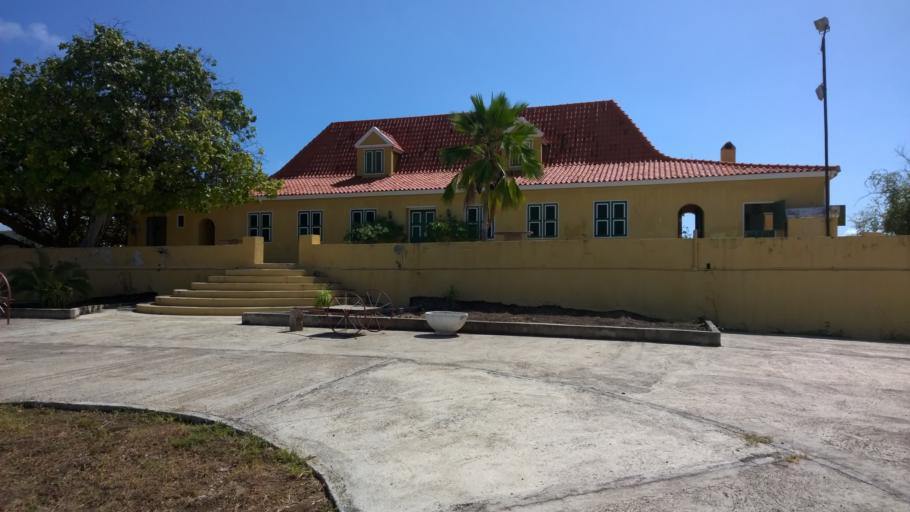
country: CW
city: Dorp Soto
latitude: 12.2749
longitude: -69.1144
